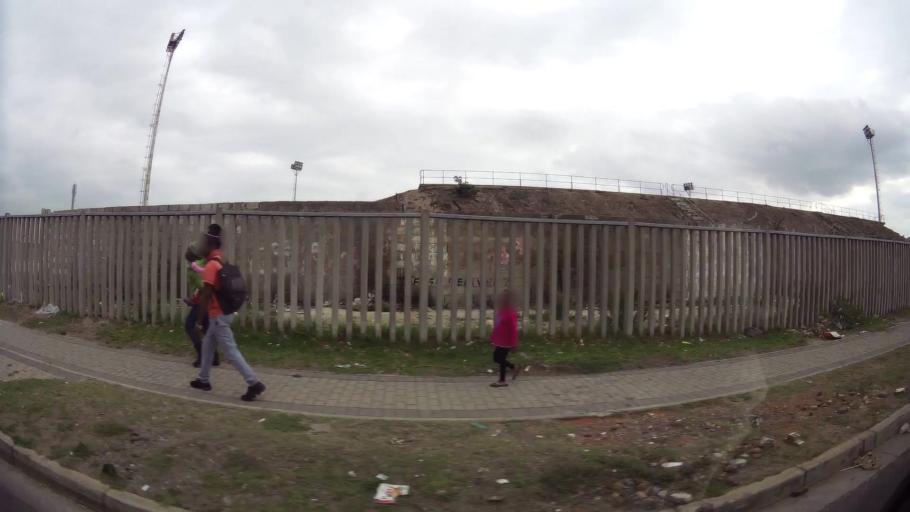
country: ZA
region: Eastern Cape
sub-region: Nelson Mandela Bay Metropolitan Municipality
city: Port Elizabeth
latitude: -33.8847
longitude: 25.5961
